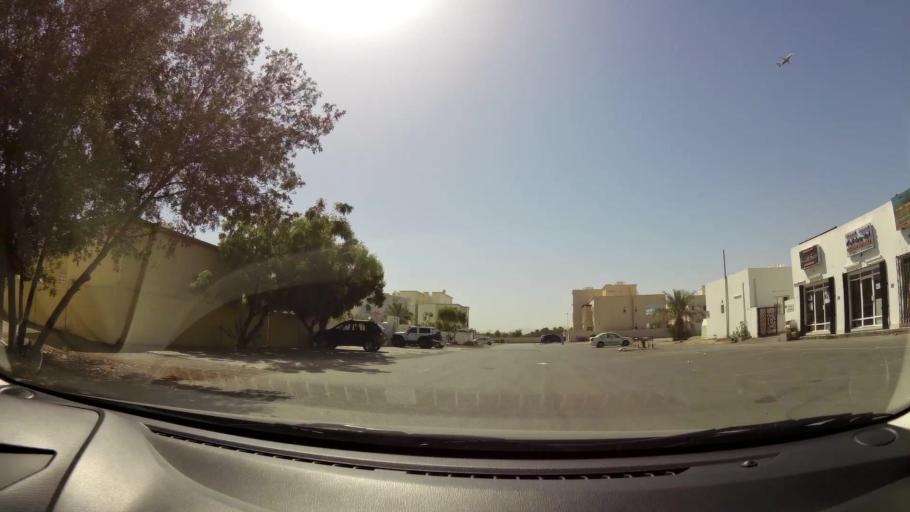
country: OM
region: Muhafazat Masqat
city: As Sib al Jadidah
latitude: 23.6089
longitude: 58.2408
